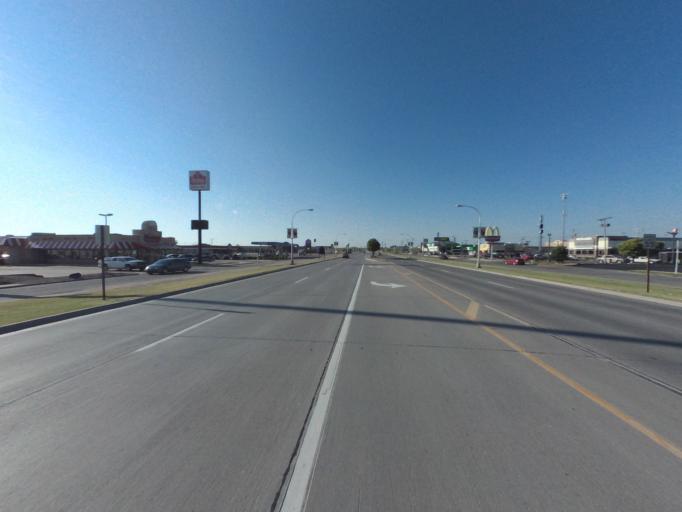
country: US
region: Kansas
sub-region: Ellis County
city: Hays
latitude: 38.8949
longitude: -99.3178
